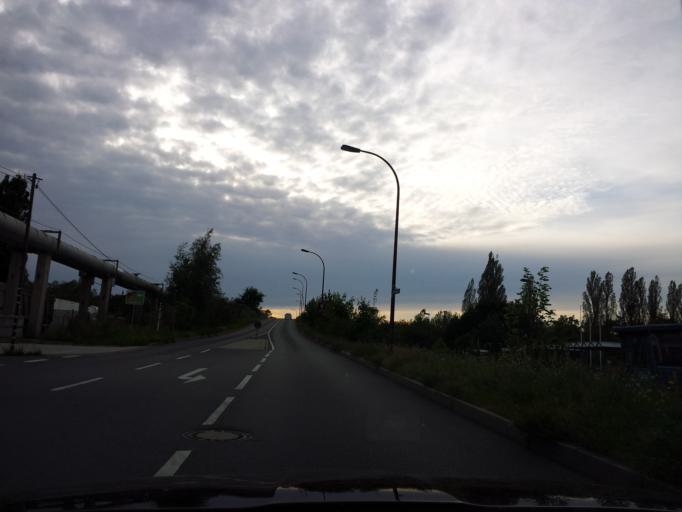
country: DE
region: Brandenburg
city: Ludwigsfelde
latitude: 52.3150
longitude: 13.2746
